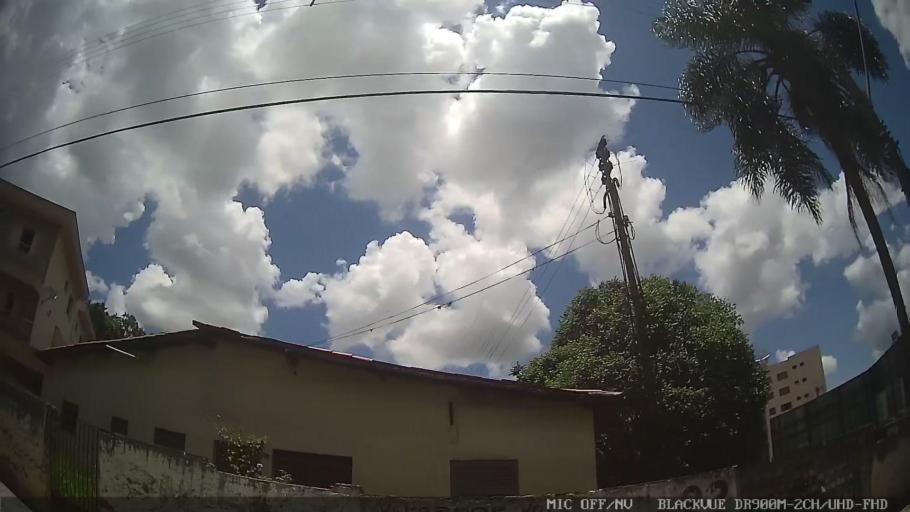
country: BR
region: Sao Paulo
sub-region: Serra Negra
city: Serra Negra
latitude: -22.6150
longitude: -46.6969
